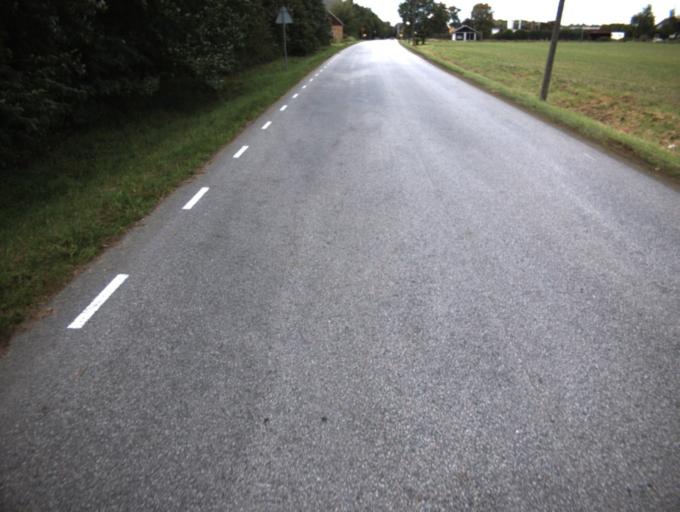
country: SE
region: Skane
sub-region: Helsingborg
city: Odakra
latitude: 56.0817
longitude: 12.7561
